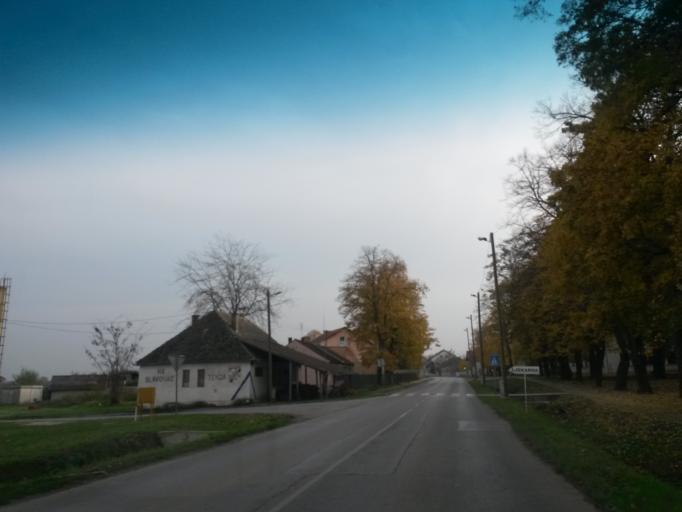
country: HR
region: Osjecko-Baranjska
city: Tenja
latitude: 45.5047
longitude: 18.7425
